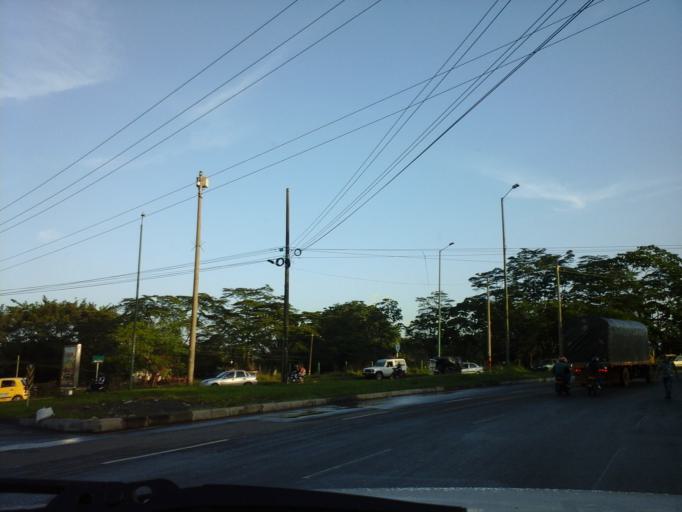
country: CO
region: Meta
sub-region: Villavicencio
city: Villavicencio
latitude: 4.1202
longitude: -73.6160
